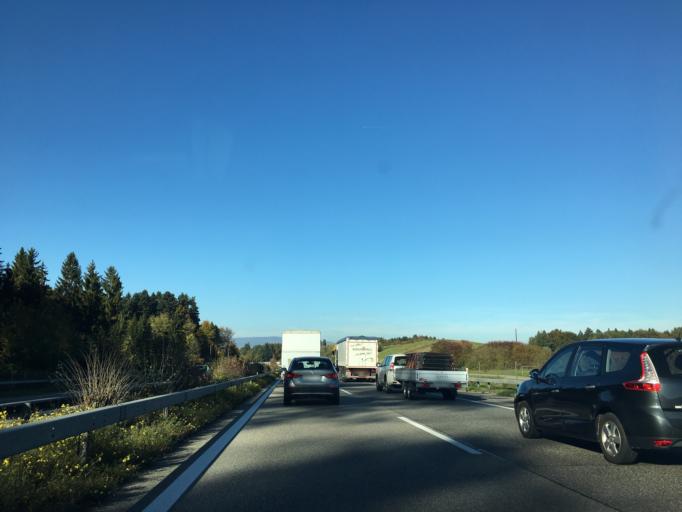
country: CH
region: Bern
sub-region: Emmental District
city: Koppigen
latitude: 47.1419
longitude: 7.5893
